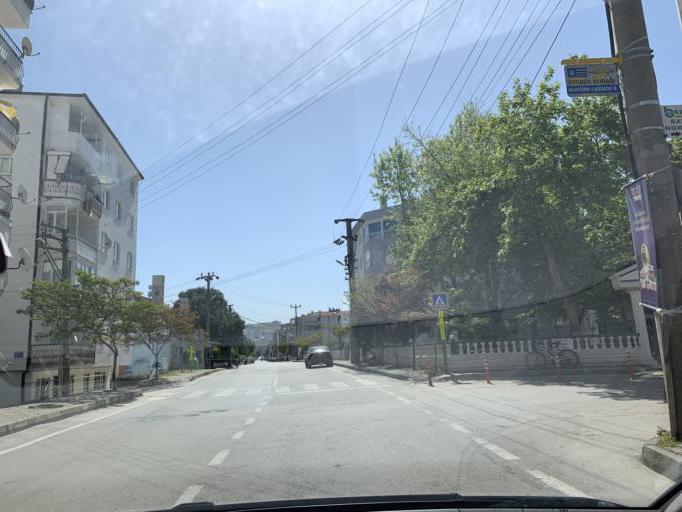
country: TR
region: Bursa
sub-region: Mudanya
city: Mudanya
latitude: 40.3583
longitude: 28.9157
